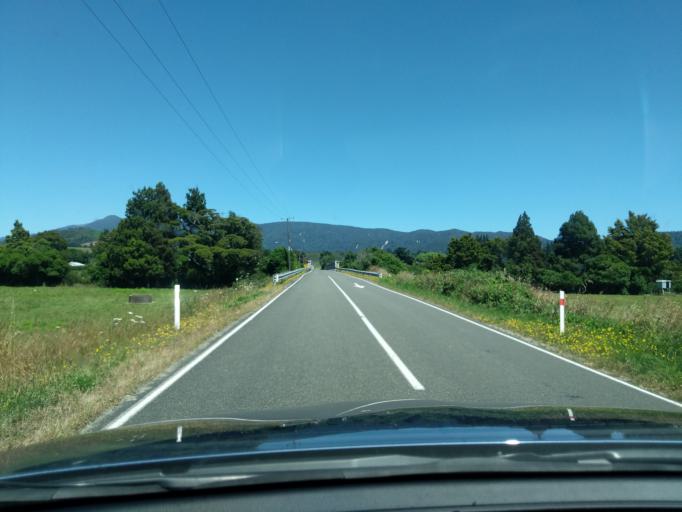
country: NZ
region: Tasman
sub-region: Tasman District
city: Takaka
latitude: -40.7292
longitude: 172.6304
